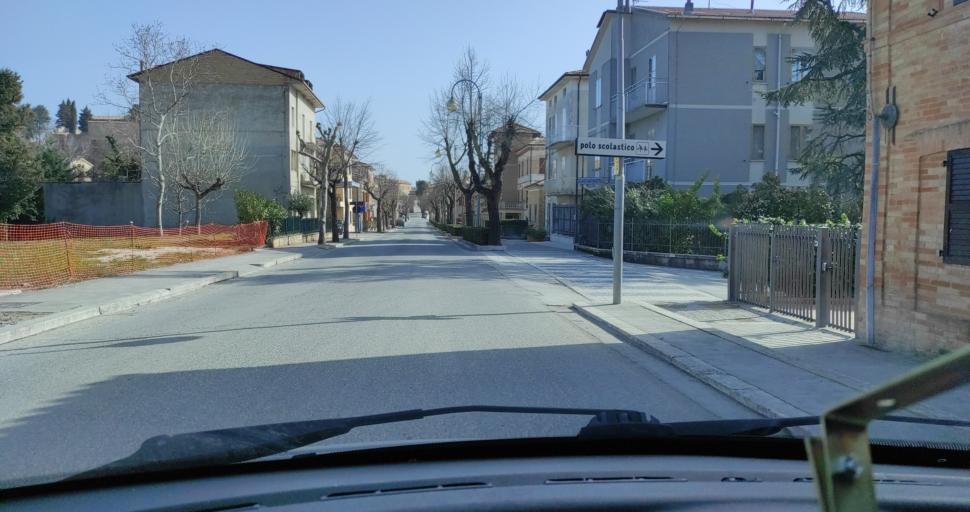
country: IT
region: The Marches
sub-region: Provincia di Macerata
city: Loro Piceno
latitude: 43.1647
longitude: 13.4125
